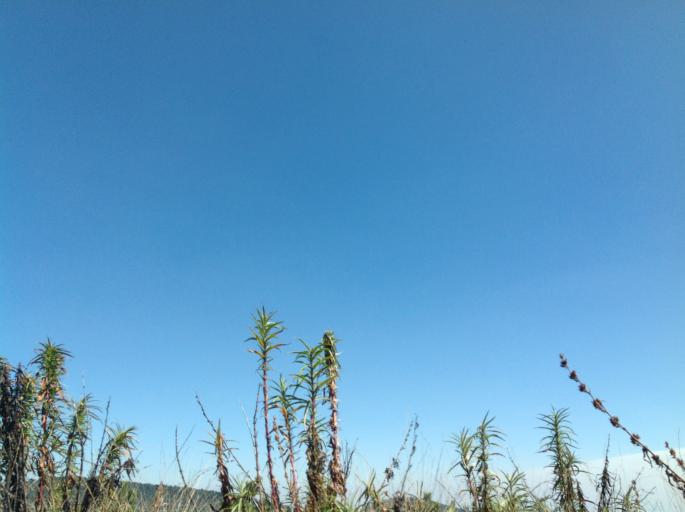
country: MX
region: Mexico
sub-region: Amecameca
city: San Diego Huehuecalco
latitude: 19.1106
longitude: -98.6443
